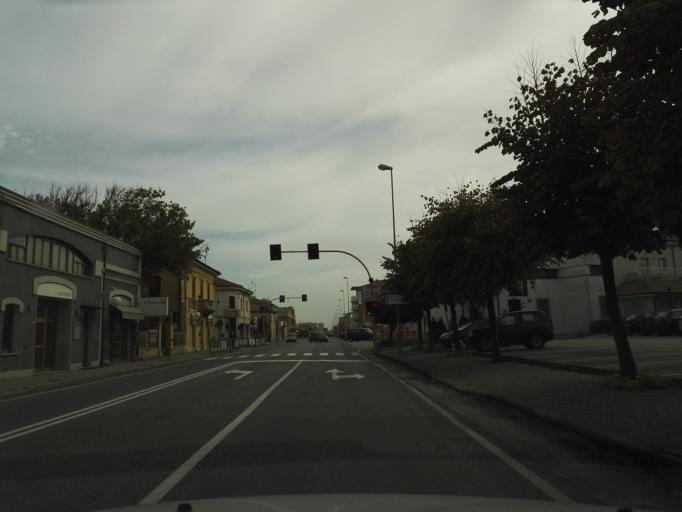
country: IT
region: The Marches
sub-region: Provincia di Pesaro e Urbino
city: Marotta
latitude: 43.7681
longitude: 13.1393
